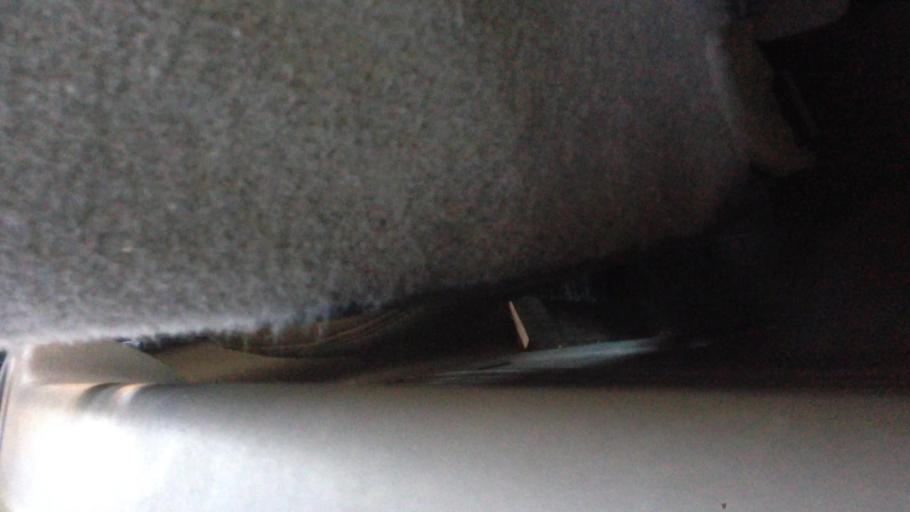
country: US
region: New York
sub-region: Dutchess County
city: Tivoli
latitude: 42.0814
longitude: -73.8303
